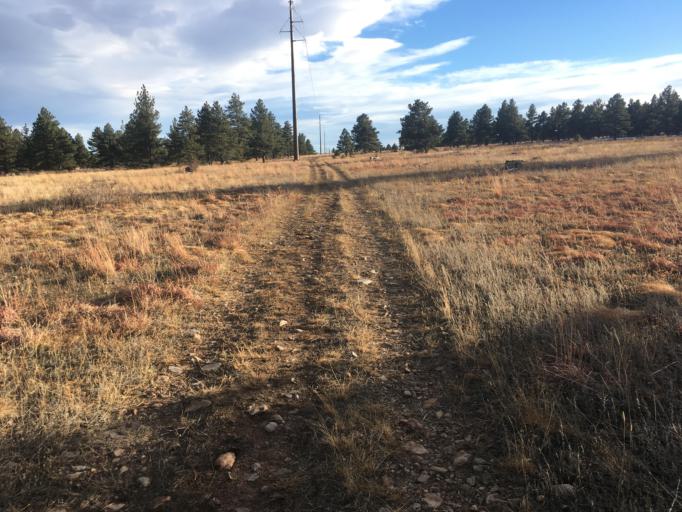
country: US
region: Colorado
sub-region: Boulder County
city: Superior
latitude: 39.9185
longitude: -105.2530
